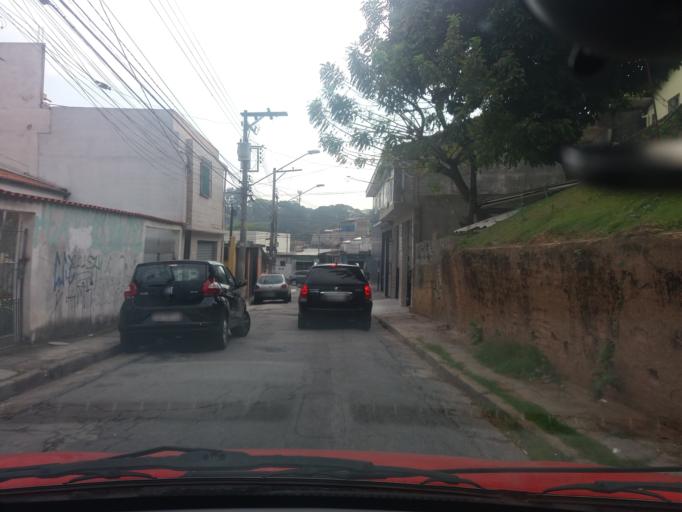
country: BR
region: Sao Paulo
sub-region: Taboao Da Serra
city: Taboao da Serra
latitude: -23.5995
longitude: -46.7370
